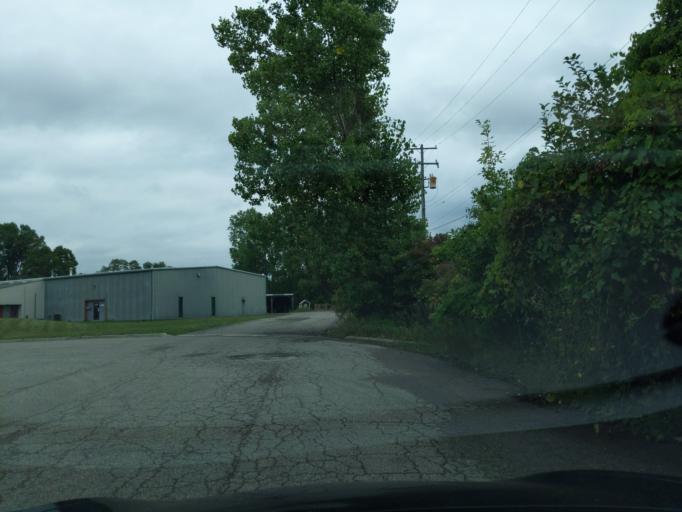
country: US
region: Michigan
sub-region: Ingham County
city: Holt
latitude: 42.6847
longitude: -84.5327
